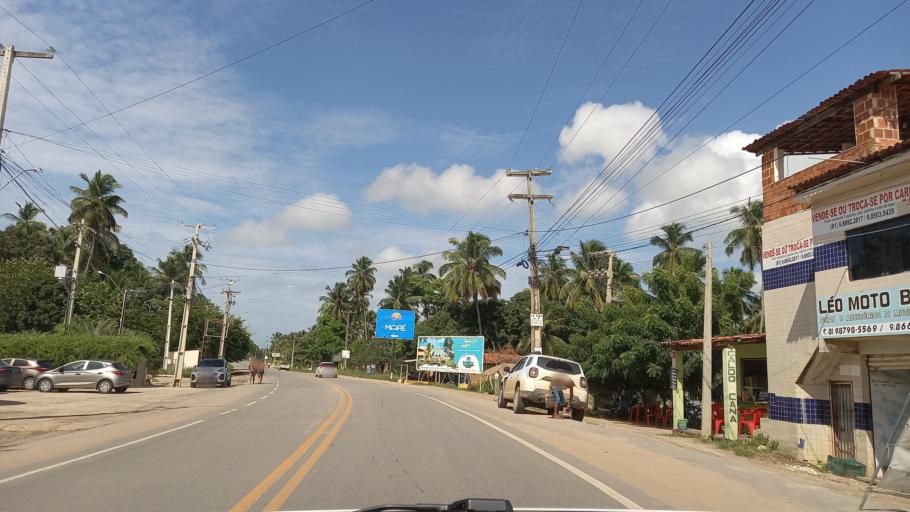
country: BR
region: Pernambuco
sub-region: Sao Jose Da Coroa Grande
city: Sao Jose da Coroa Grande
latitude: -8.9305
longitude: -35.1667
